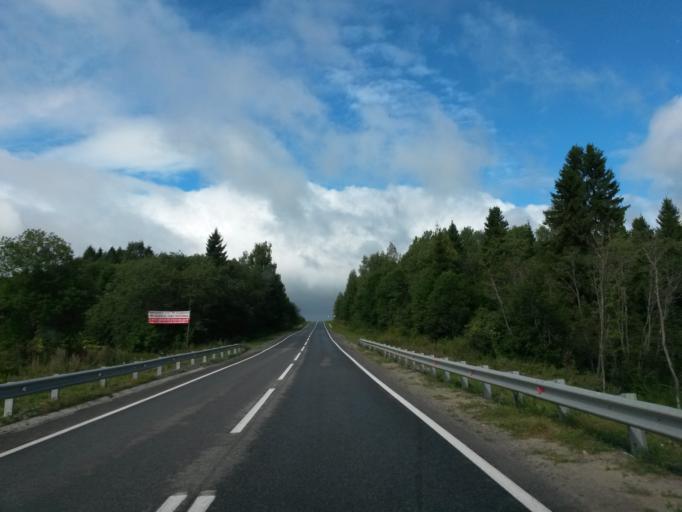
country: RU
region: Jaroslavl
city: Konstantinovskiy
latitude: 57.8143
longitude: 39.7201
